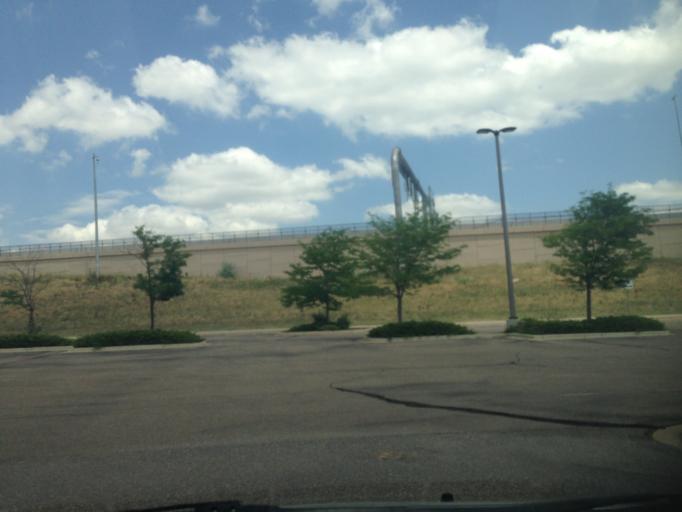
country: US
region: Colorado
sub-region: Broomfield County
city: Broomfield
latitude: 39.8903
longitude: -105.0757
